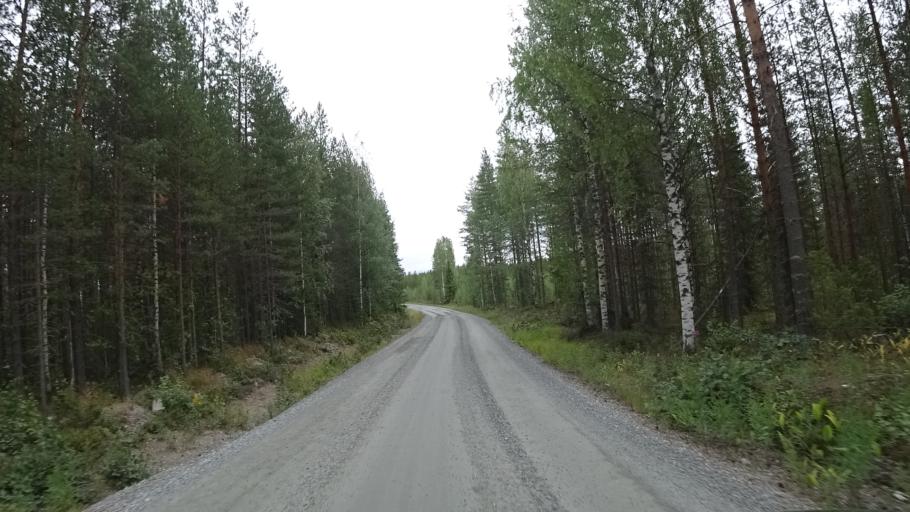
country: FI
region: North Karelia
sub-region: Pielisen Karjala
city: Lieksa
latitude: 63.3677
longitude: 30.3864
